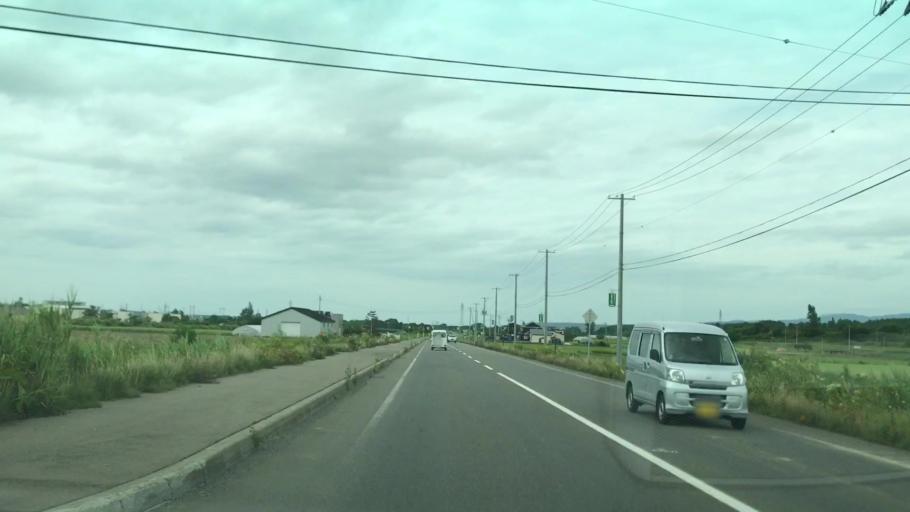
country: JP
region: Hokkaido
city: Iwanai
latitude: 42.9807
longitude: 140.6224
